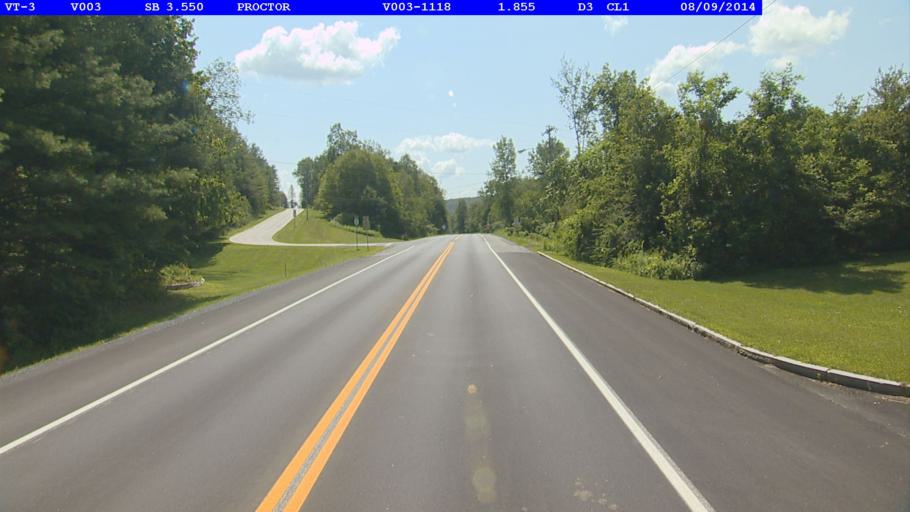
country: US
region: Vermont
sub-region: Rutland County
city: West Rutland
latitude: 43.6504
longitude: -73.0326
